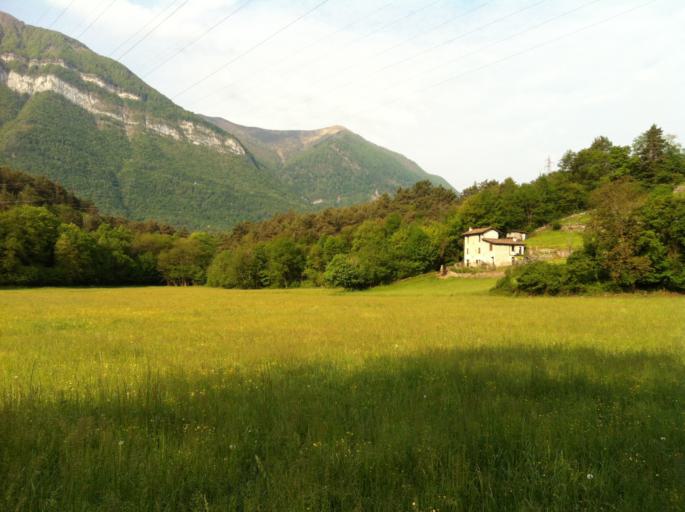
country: IT
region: Lombardy
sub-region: Provincia di Como
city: Grandola ed Uniti
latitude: 46.0294
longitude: 9.2233
